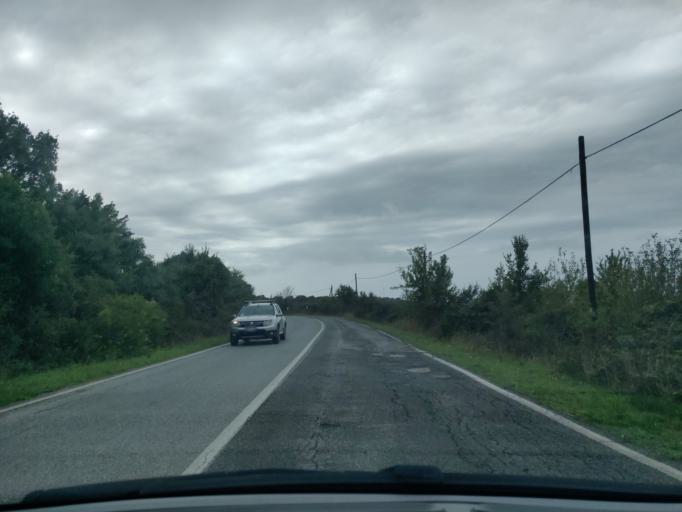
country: IT
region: Latium
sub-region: Citta metropolitana di Roma Capitale
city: Allumiere
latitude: 42.1203
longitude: 11.8621
